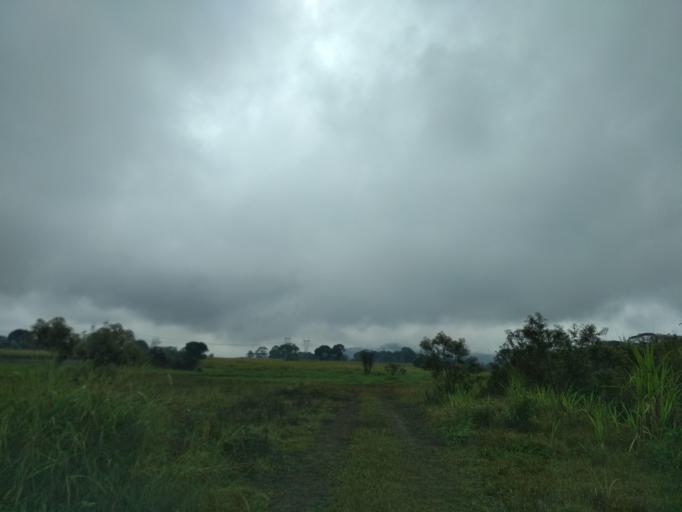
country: MX
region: Veracruz
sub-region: Amatlan de los Reyes
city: Centro de Readaptacion Social
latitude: 18.8357
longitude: -96.9376
